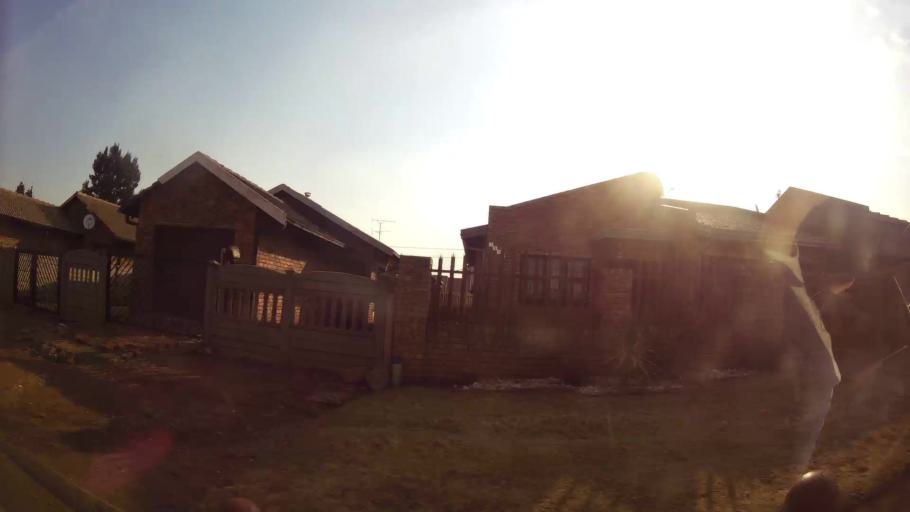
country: ZA
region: Gauteng
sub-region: Ekurhuleni Metropolitan Municipality
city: Germiston
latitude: -26.3651
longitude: 28.2069
